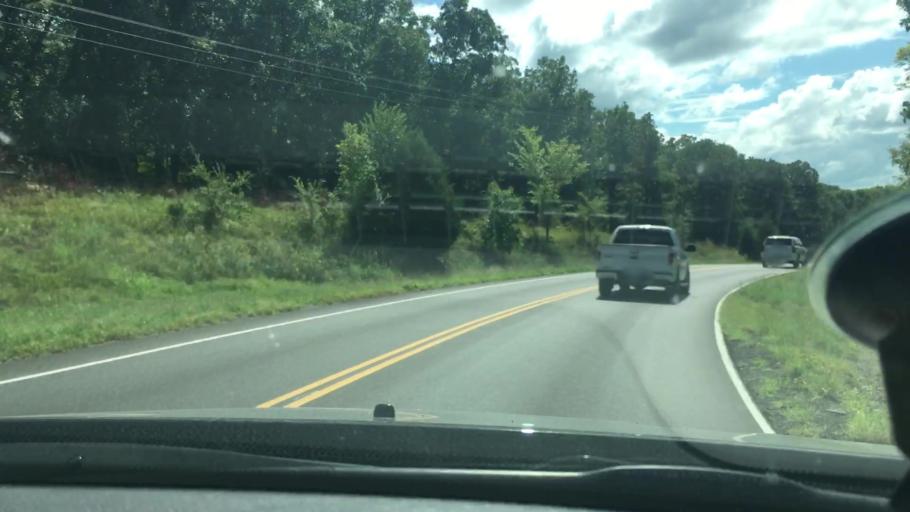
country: US
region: Oklahoma
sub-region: Sequoyah County
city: Vian
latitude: 35.6491
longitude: -94.9546
